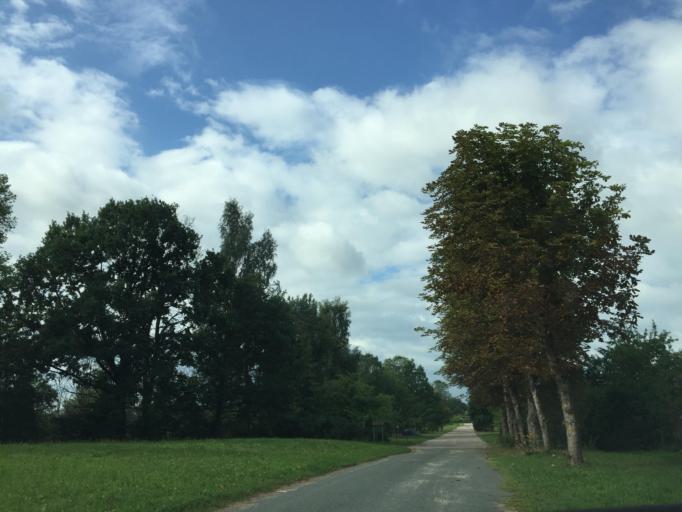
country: LV
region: Kegums
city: Kegums
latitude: 56.8030
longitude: 24.7470
